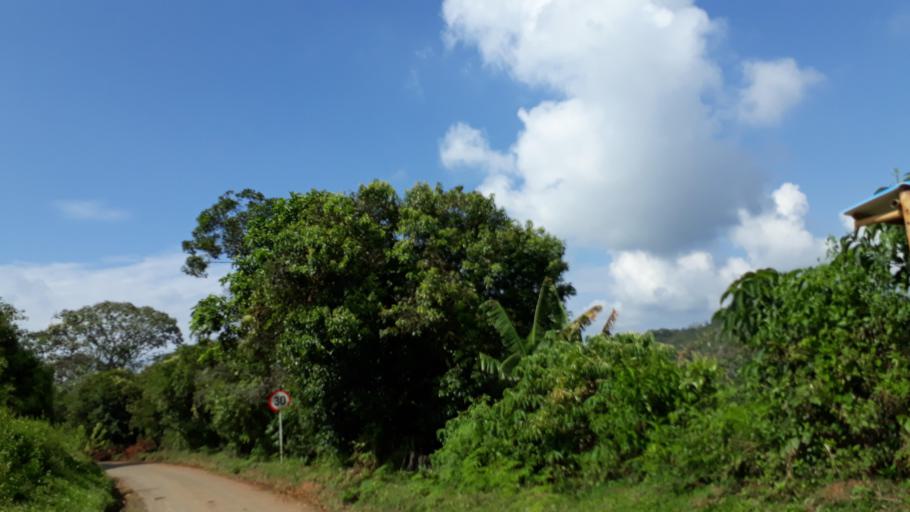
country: CO
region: Valle del Cauca
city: Jamundi
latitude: 3.2678
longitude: -76.6248
